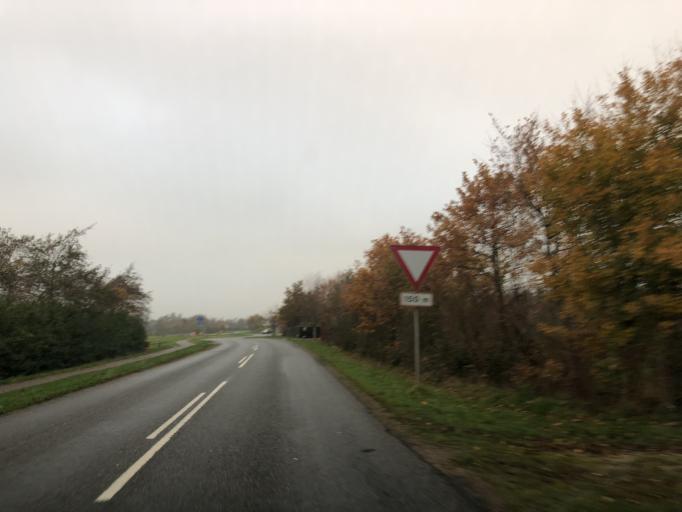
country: DK
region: Central Jutland
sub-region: Herning Kommune
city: Vildbjerg
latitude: 56.2200
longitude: 8.7378
